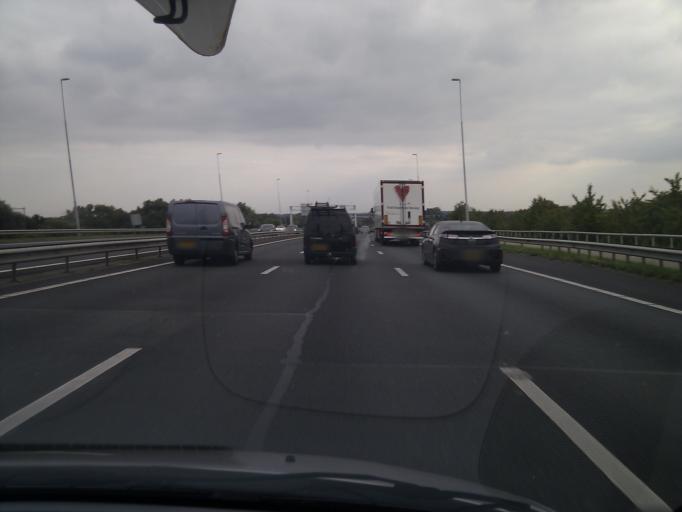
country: NL
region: Gelderland
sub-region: Gemeente Zaltbommel
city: Zaltbommel
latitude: 51.8163
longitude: 5.2603
